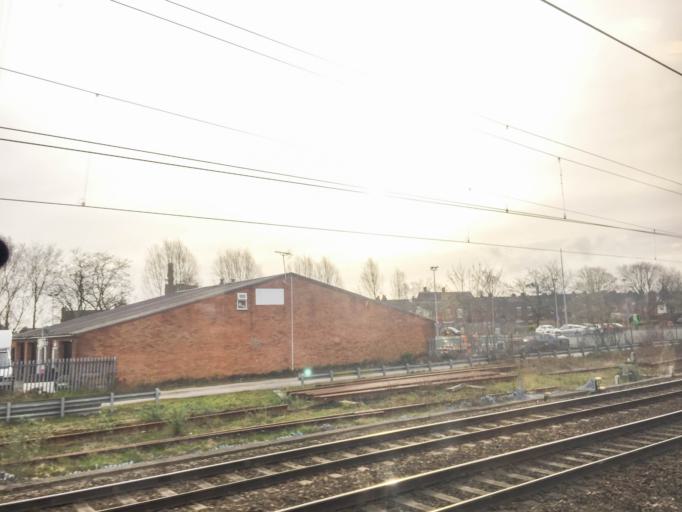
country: GB
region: England
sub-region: Cheshire East
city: Crewe
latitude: 53.0997
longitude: -2.4386
